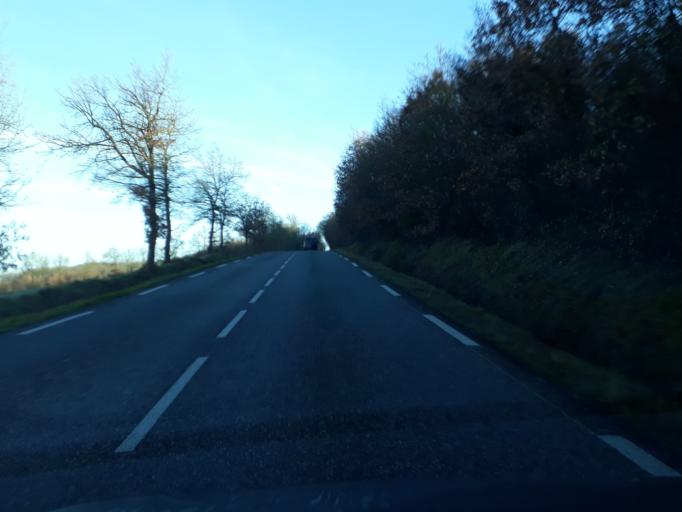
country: FR
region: Midi-Pyrenees
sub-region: Departement du Gers
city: Pujaudran
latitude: 43.5722
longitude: 1.1287
